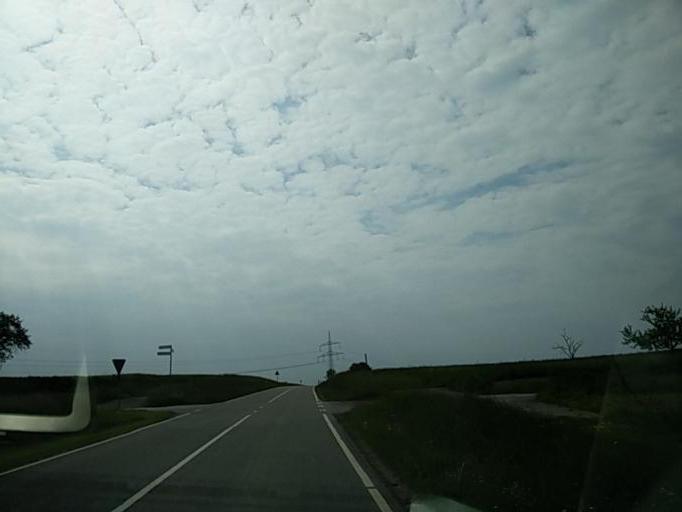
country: DE
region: Baden-Wuerttemberg
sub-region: Tuebingen Region
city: Hirrlingen
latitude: 48.4290
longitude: 8.8780
